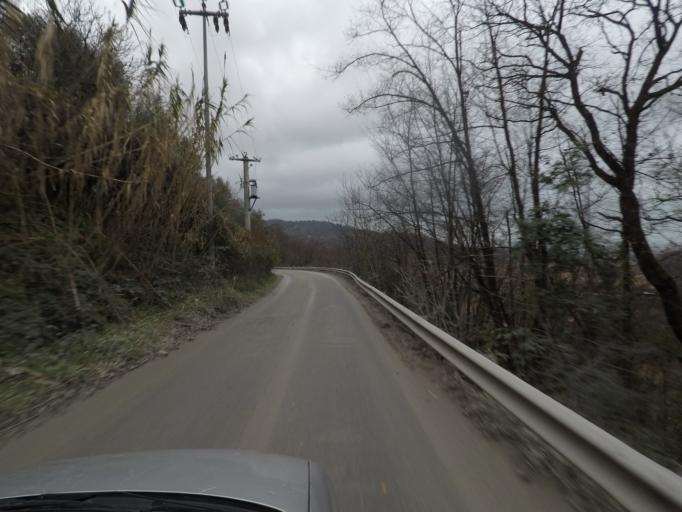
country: IT
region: Tuscany
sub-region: Provincia di Massa-Carrara
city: Carrara
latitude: 44.0851
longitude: 10.1047
